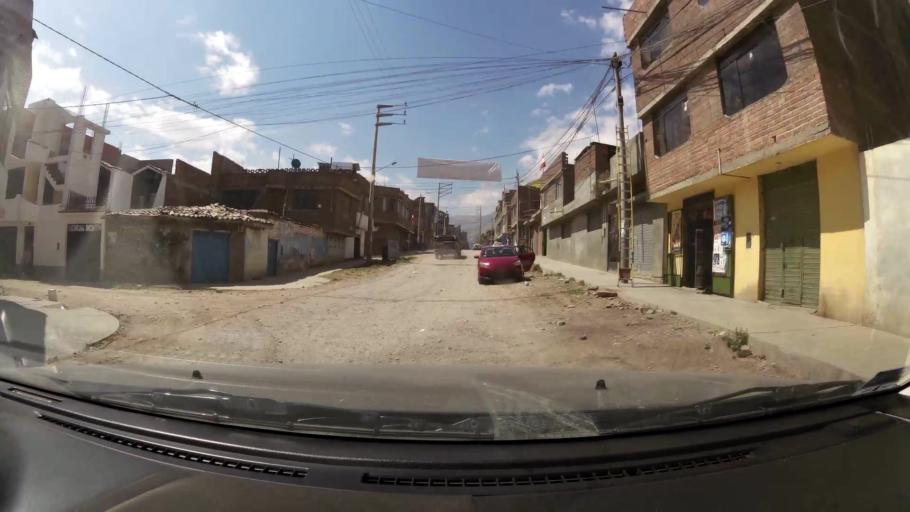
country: PE
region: Junin
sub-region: Provincia de Huancayo
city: El Tambo
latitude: -12.0672
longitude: -75.2239
